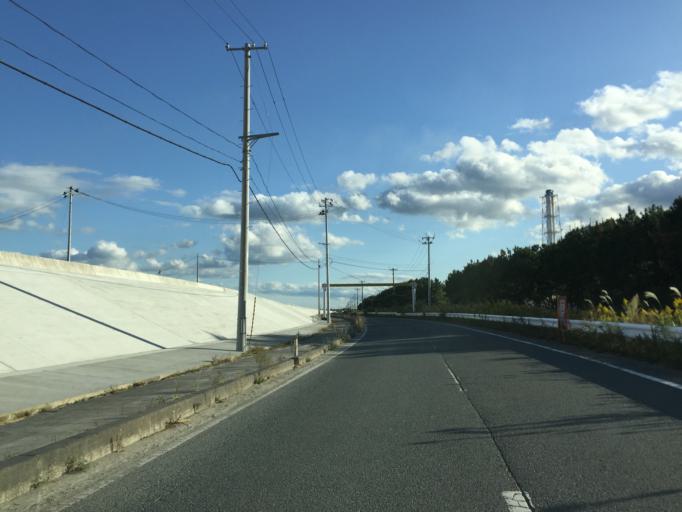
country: JP
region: Miyagi
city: Marumori
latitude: 37.8504
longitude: 140.9470
